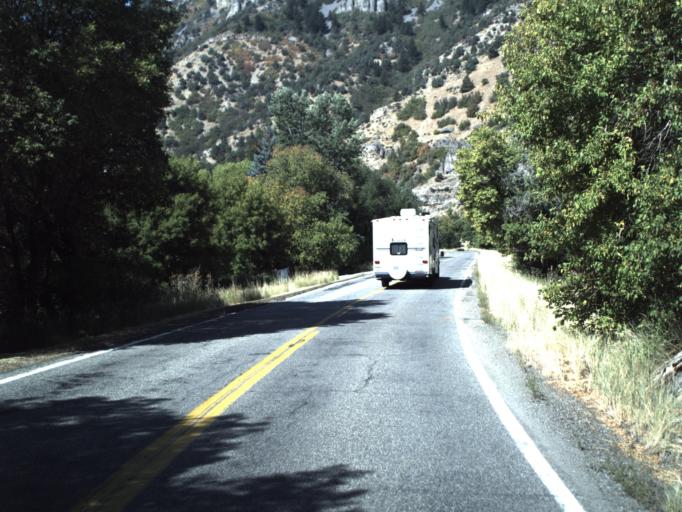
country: US
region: Utah
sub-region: Cache County
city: Millville
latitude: 41.6294
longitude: -111.7162
